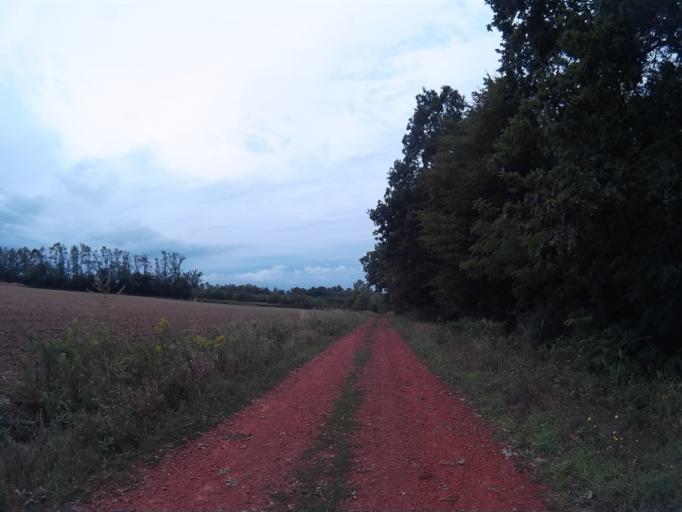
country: HU
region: Zala
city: Zalalovo
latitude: 46.7671
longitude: 16.5132
